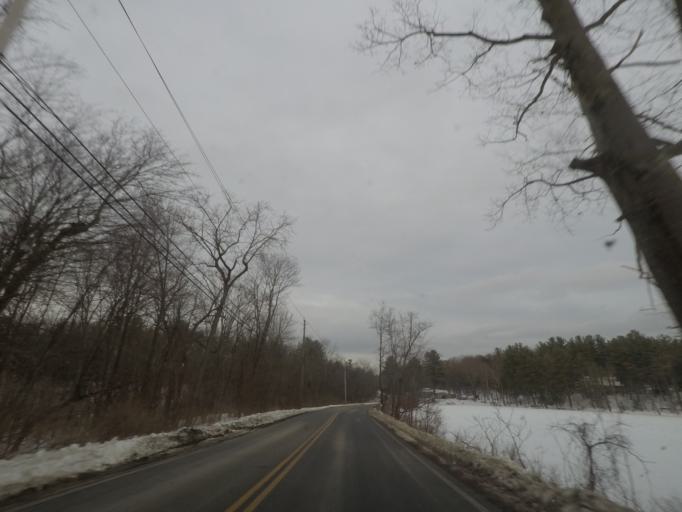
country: US
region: New York
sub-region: Rensselaer County
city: Averill Park
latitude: 42.6195
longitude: -73.5675
